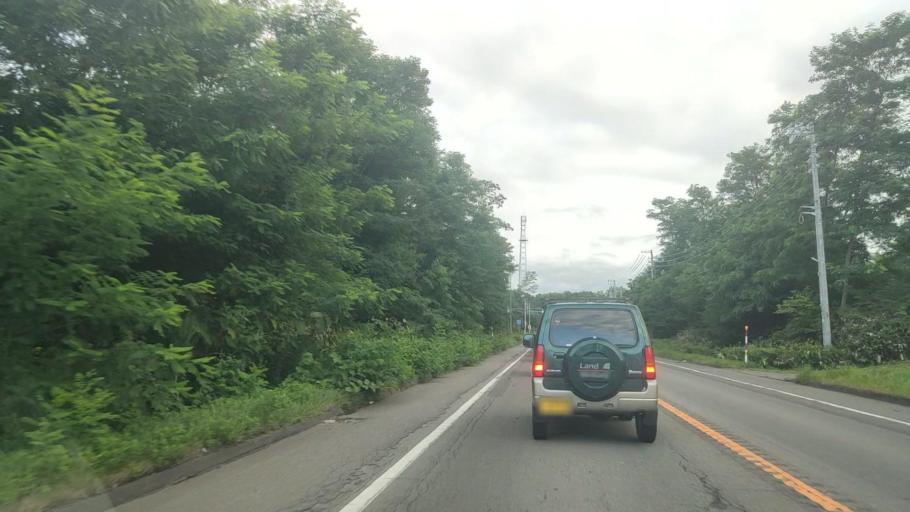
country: JP
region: Hokkaido
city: Nanae
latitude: 42.0683
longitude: 140.6032
